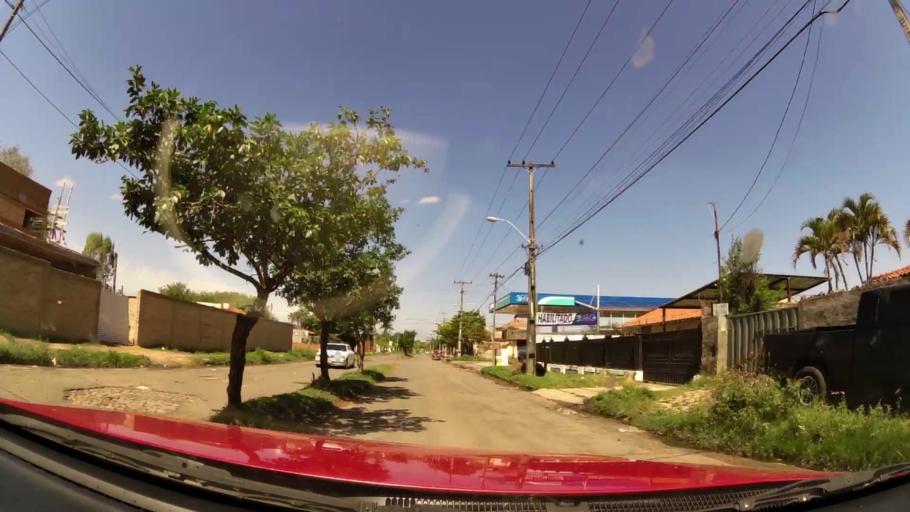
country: PY
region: Central
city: Colonia Mariano Roque Alonso
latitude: -25.2230
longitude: -57.5425
